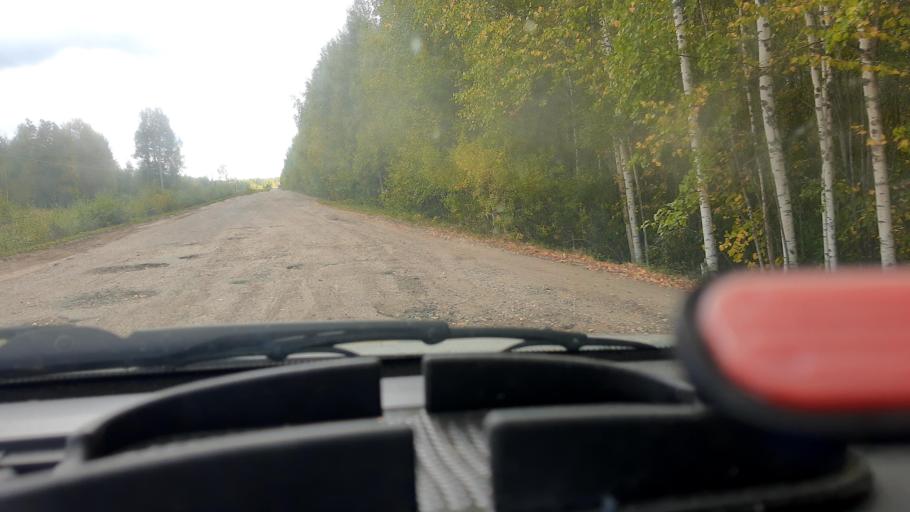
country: RU
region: Mariy-El
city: Kilemary
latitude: 56.8912
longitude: 46.7555
